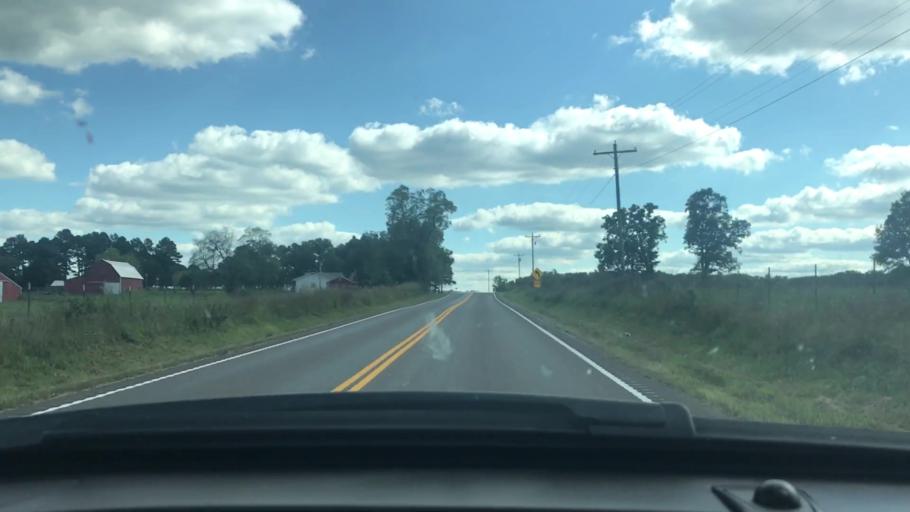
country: US
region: Missouri
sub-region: Wright County
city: Mountain Grove
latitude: 37.2374
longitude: -92.3006
